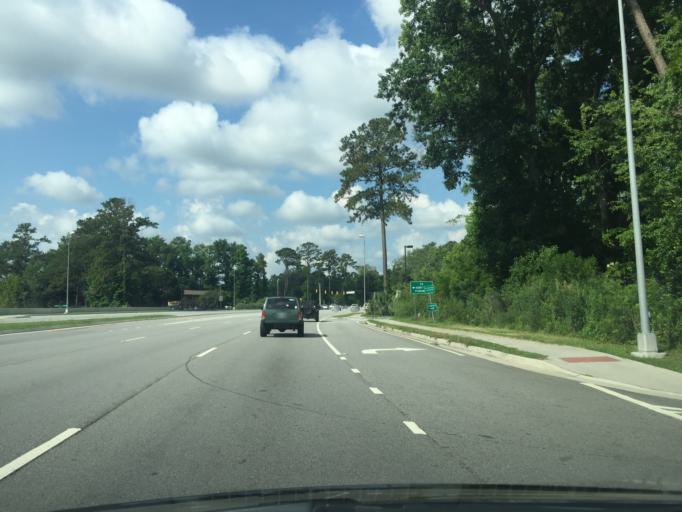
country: US
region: Georgia
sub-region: Chatham County
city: Montgomery
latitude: 31.9814
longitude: -81.1339
